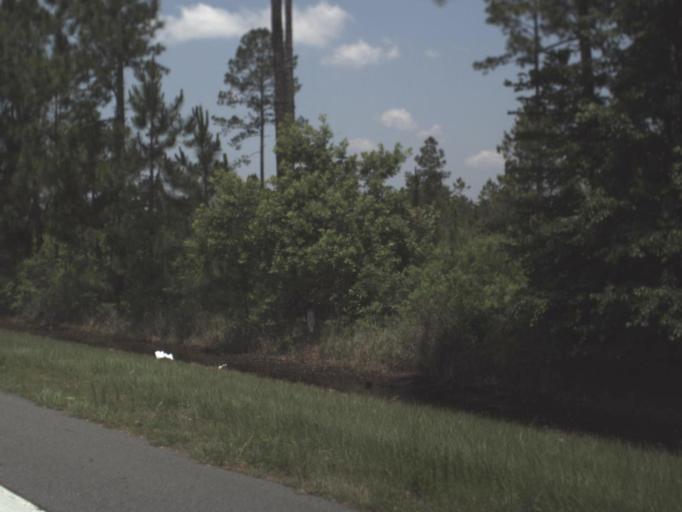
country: US
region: Florida
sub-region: Duval County
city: Baldwin
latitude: 30.2066
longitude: -81.9754
